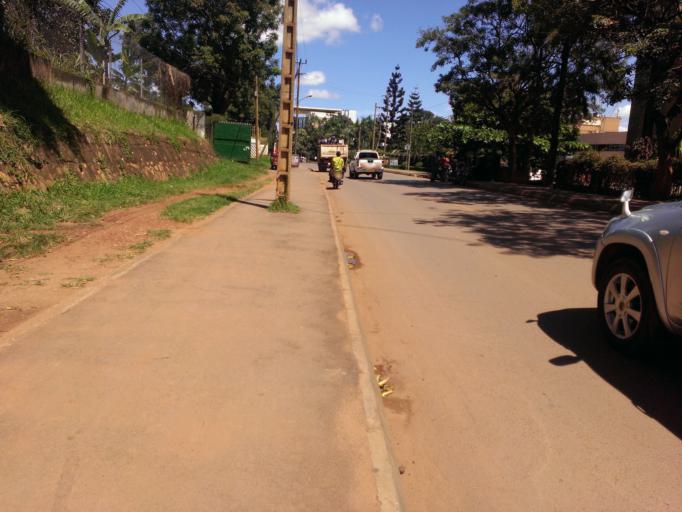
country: UG
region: Central Region
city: Kampala Central Division
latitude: 0.3244
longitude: 32.5771
